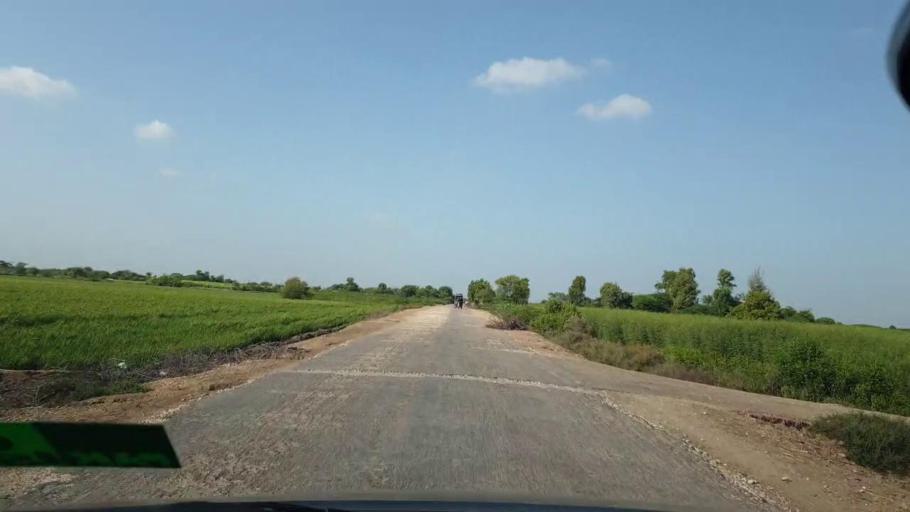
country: PK
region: Sindh
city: Tando Bago
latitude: 24.7086
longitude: 69.1923
